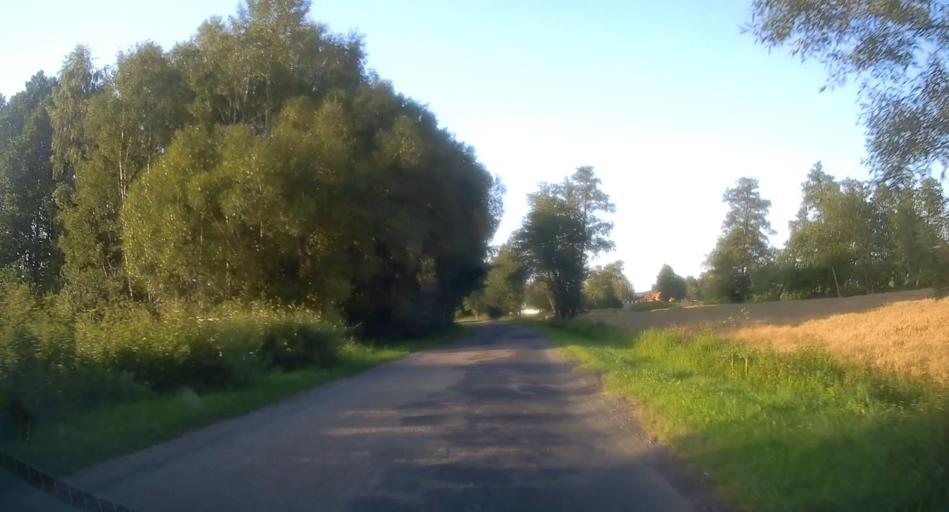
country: PL
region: Lodz Voivodeship
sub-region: Powiat skierniewicki
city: Kaweczyn Nowy
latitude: 51.8960
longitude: 20.2977
